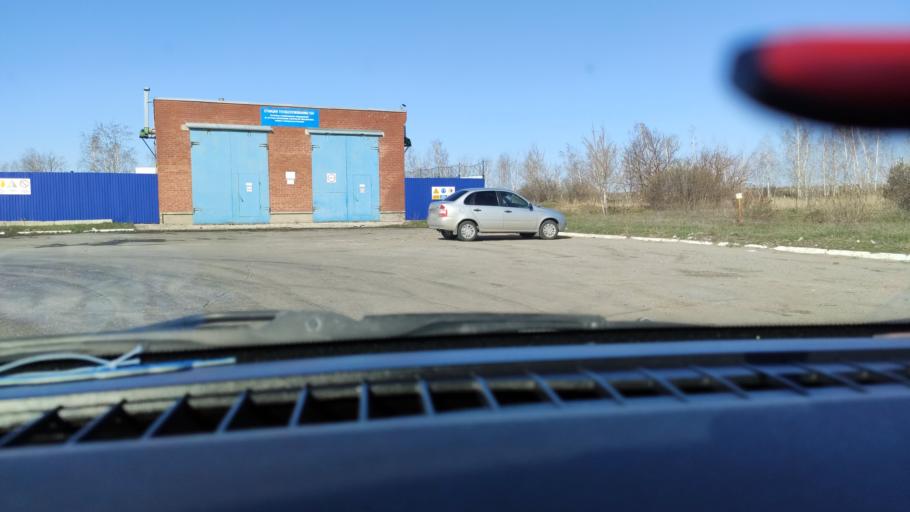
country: RU
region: Samara
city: Syzran'
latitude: 53.2056
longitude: 48.5076
